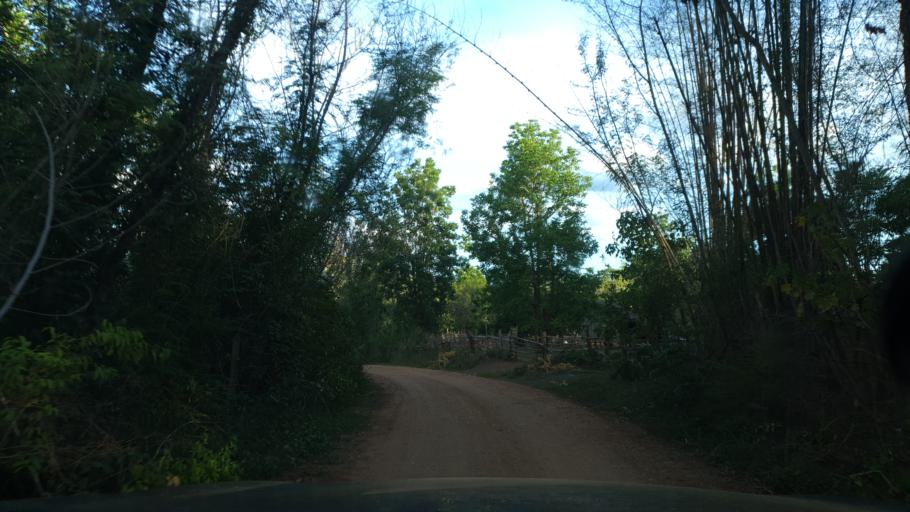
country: TH
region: Lampang
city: Sop Prap
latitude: 17.9552
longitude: 99.3480
